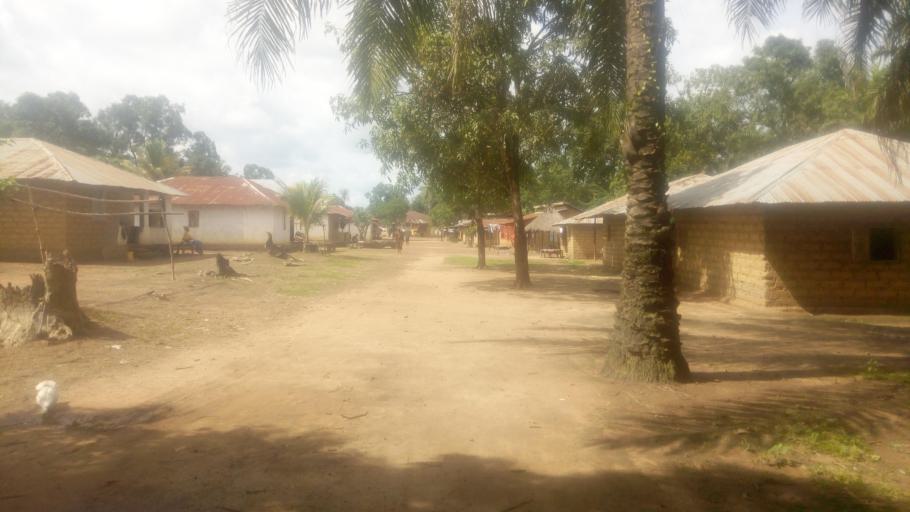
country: SL
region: Northern Province
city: Magburaka
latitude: 8.6874
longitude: -12.0642
